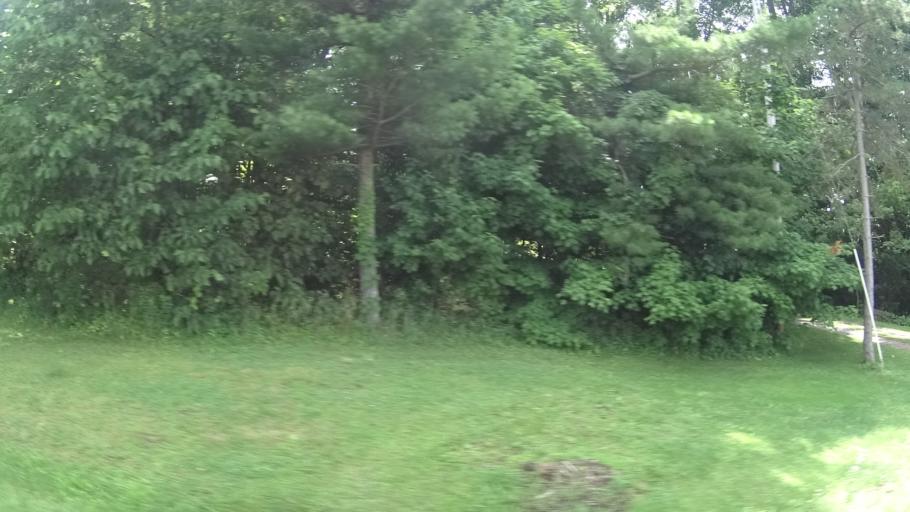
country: US
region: Ohio
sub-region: Huron County
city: Wakeman
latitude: 41.2878
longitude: -82.3975
